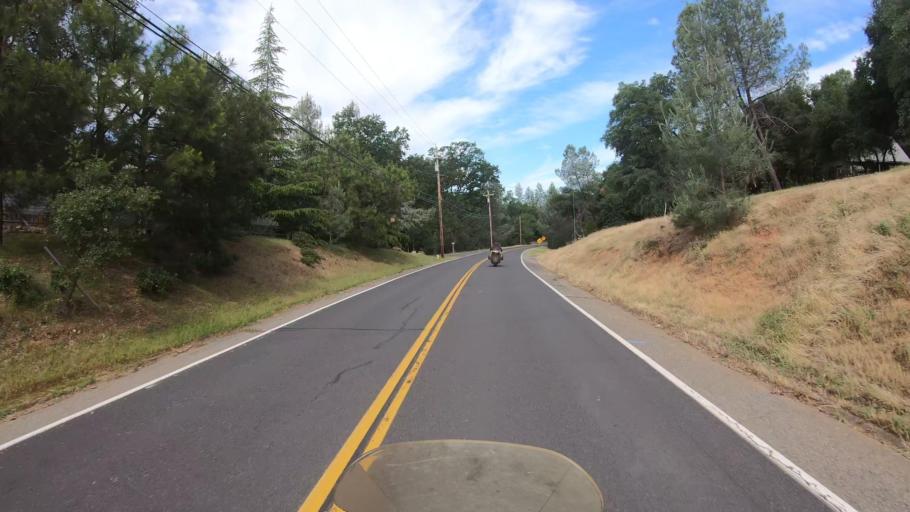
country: US
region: California
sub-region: Tuolumne County
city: Tuolumne City
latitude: 37.8592
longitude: -120.1869
